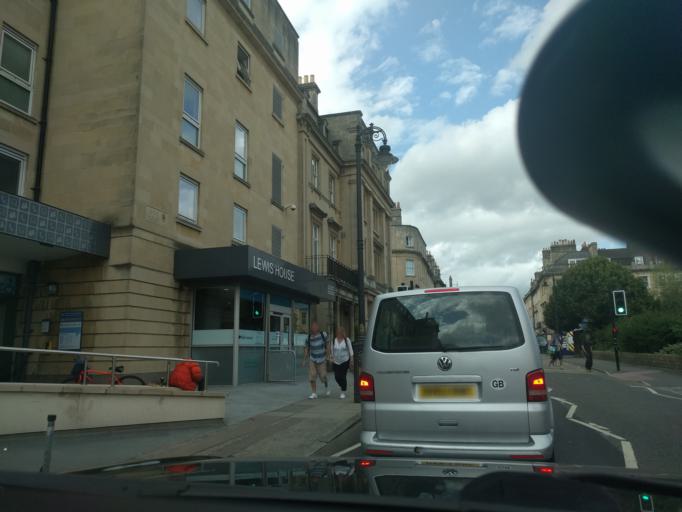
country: GB
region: England
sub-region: Bath and North East Somerset
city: Bath
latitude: 51.3794
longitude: -2.3571
